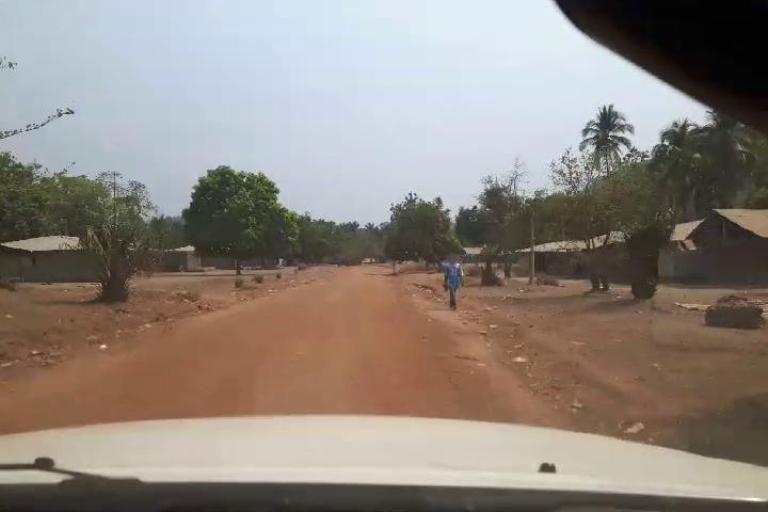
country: SL
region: Northern Province
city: Bumbuna
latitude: 9.0245
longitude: -11.7630
